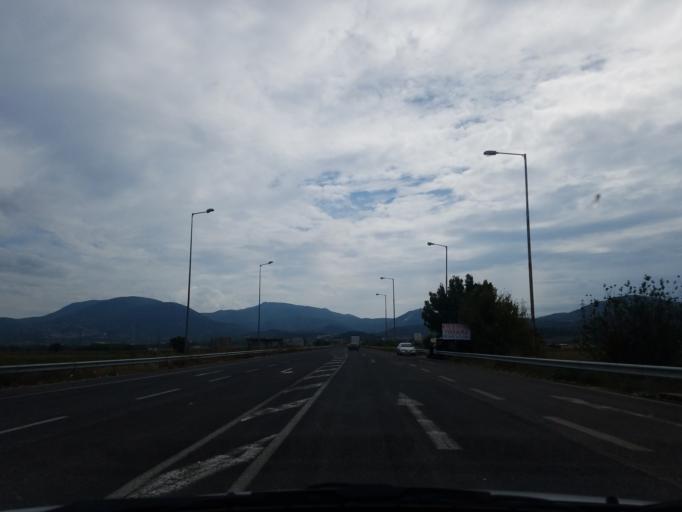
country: GR
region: Central Greece
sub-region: Nomos Fthiotidos
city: Domokos
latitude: 39.0420
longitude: 22.3528
